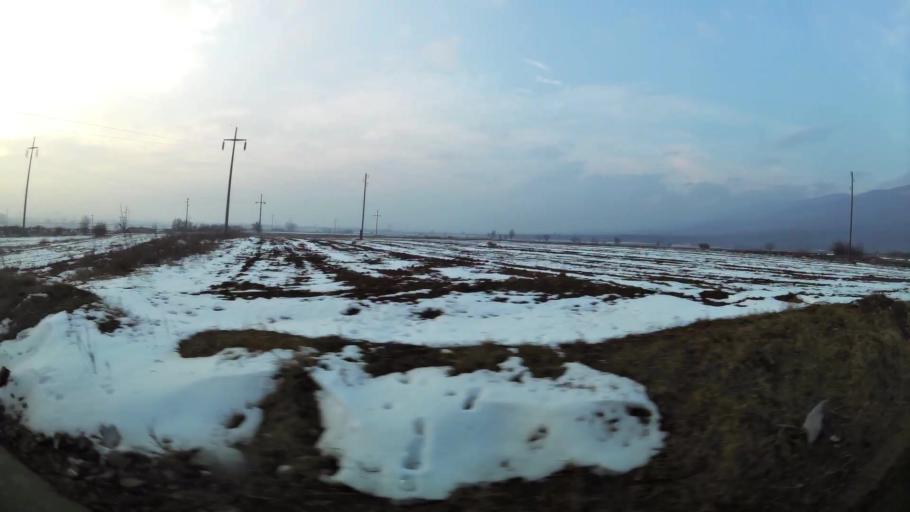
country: MK
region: Aracinovo
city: Arachinovo
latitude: 42.0259
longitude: 21.5447
